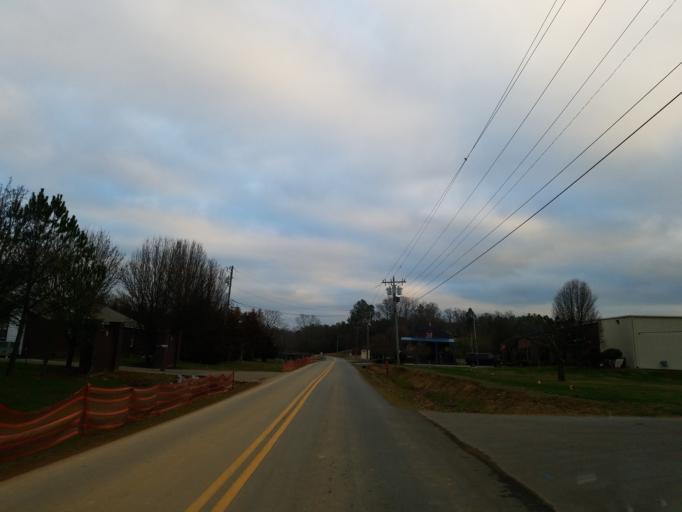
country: US
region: Georgia
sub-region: Gordon County
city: Calhoun
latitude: 34.4410
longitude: -84.9063
